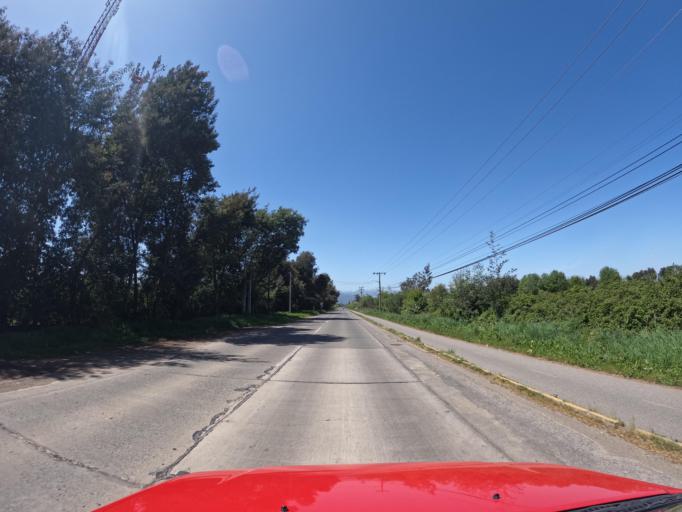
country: CL
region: Maule
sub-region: Provincia de Linares
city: Linares
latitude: -35.8310
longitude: -71.5186
